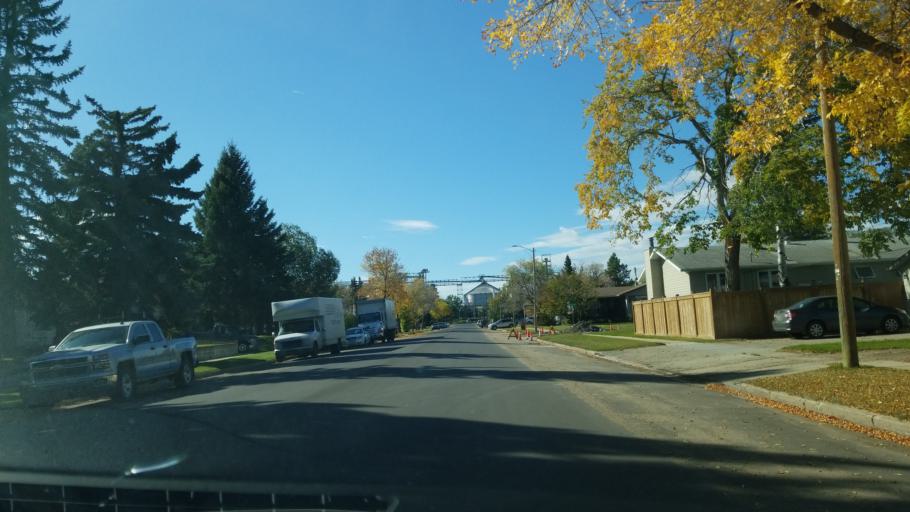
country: CA
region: Saskatchewan
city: Lloydminster
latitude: 53.2835
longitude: -110.0244
